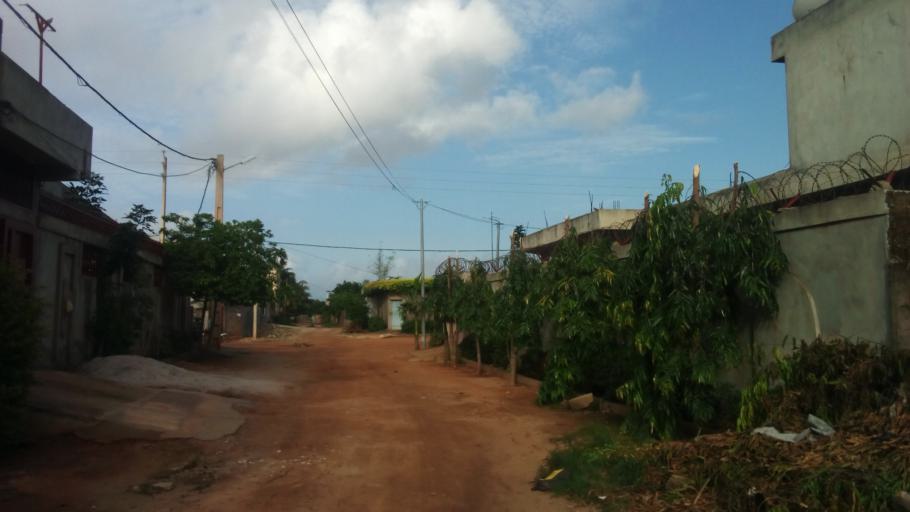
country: BJ
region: Atlantique
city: Abomey-Calavi
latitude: 6.4384
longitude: 2.3447
